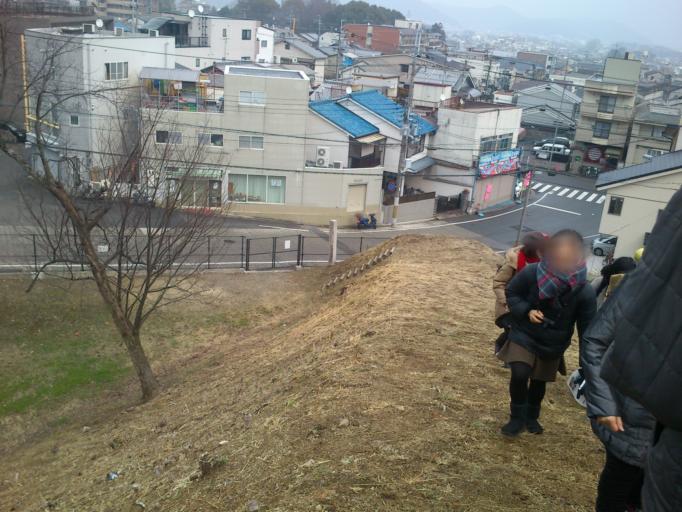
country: JP
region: Kyoto
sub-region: Kyoto-shi
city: Kamigyo-ku
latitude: 35.0518
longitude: 135.7403
